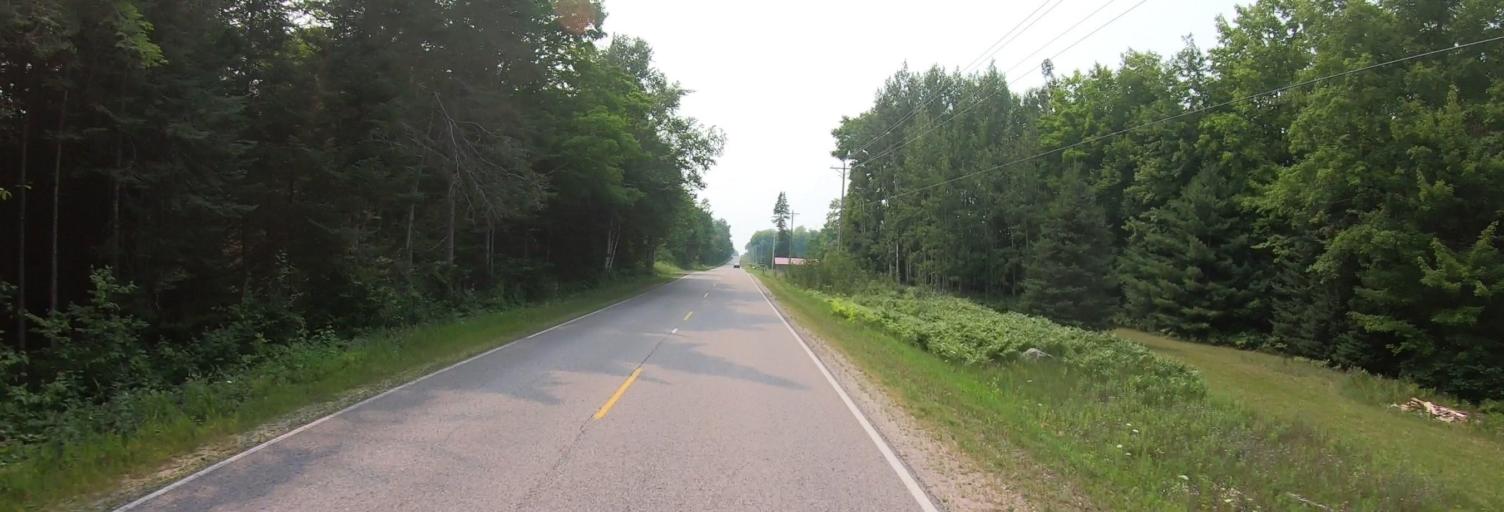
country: CA
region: Ontario
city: Thessalon
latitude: 46.0145
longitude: -84.0543
